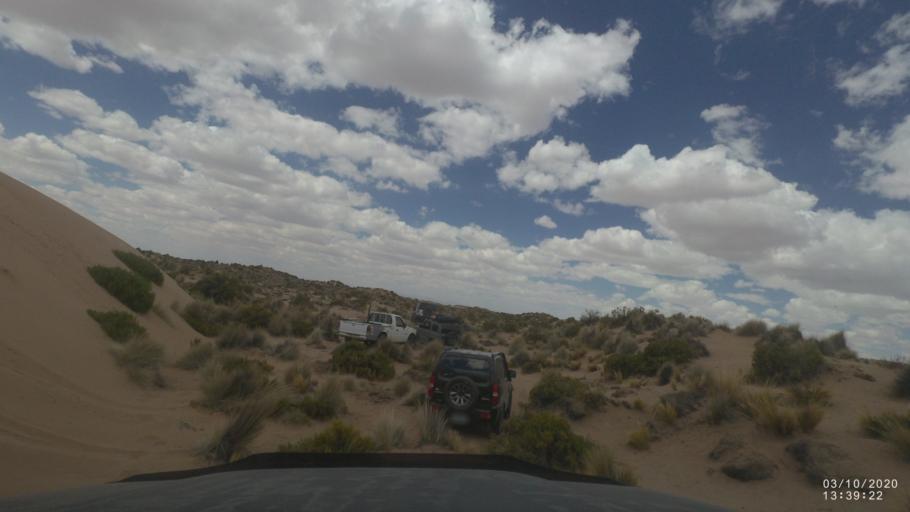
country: BO
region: Oruro
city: Poopo
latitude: -18.6913
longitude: -67.5323
